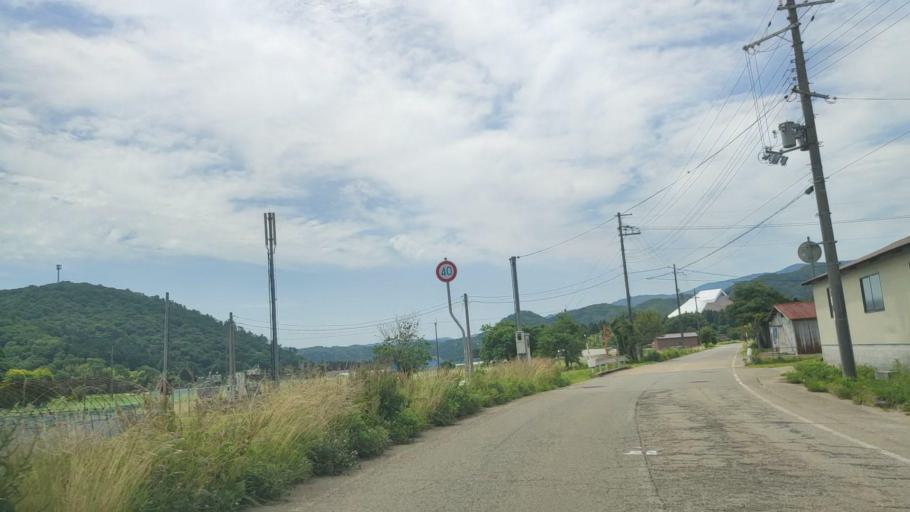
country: JP
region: Hyogo
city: Toyooka
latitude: 35.5026
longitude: 134.6911
